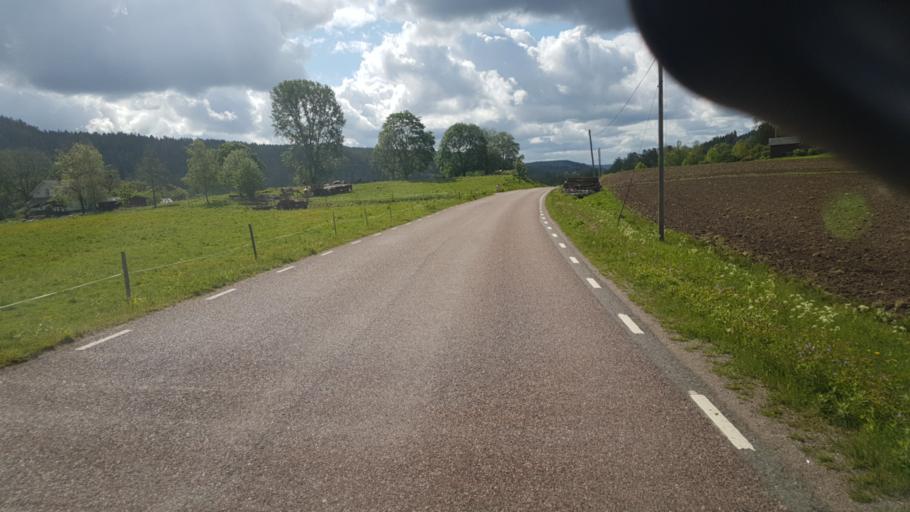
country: NO
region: Hedmark
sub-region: Eidskog
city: Skotterud
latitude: 59.7842
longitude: 12.0413
